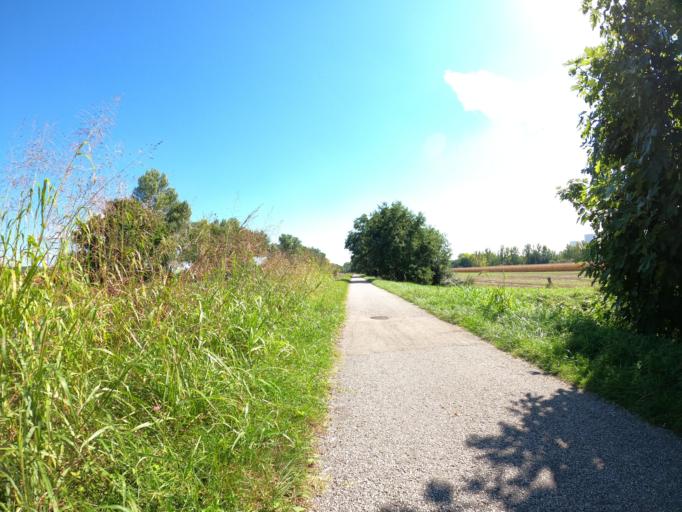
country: FR
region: Midi-Pyrenees
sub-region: Departement du Tarn-et-Garonne
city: Lamagistere
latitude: 44.1279
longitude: 0.8343
